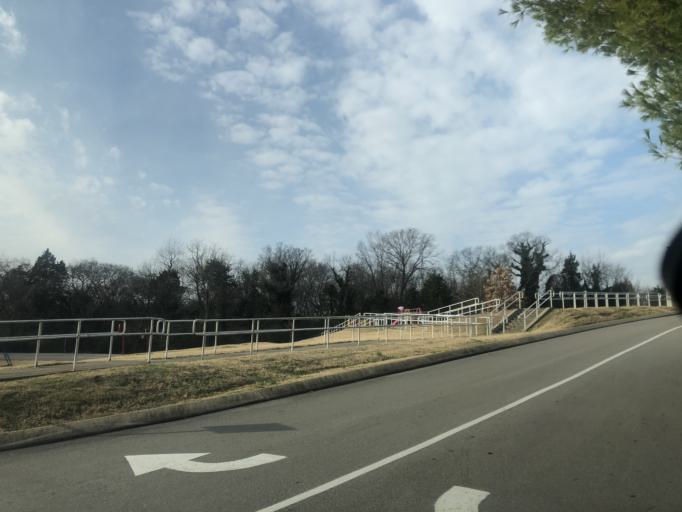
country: US
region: Tennessee
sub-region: Davidson County
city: Oak Hill
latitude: 36.1098
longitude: -86.7064
